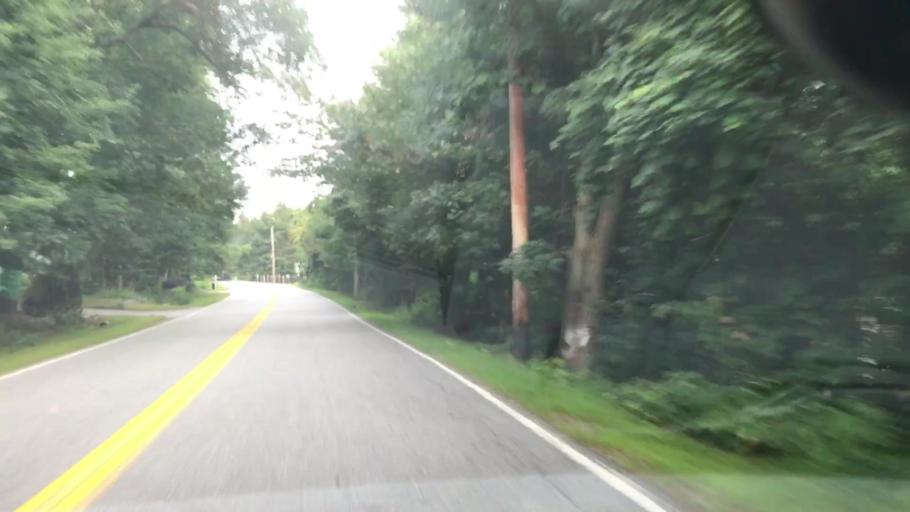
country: US
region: New Hampshire
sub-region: Hillsborough County
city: Bedford
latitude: 42.9374
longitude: -71.4807
